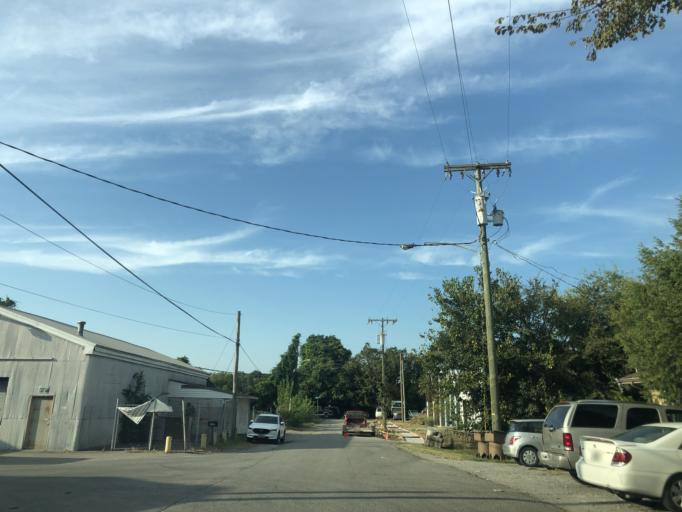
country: US
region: Tennessee
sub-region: Davidson County
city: Oak Hill
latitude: 36.1216
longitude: -86.7494
